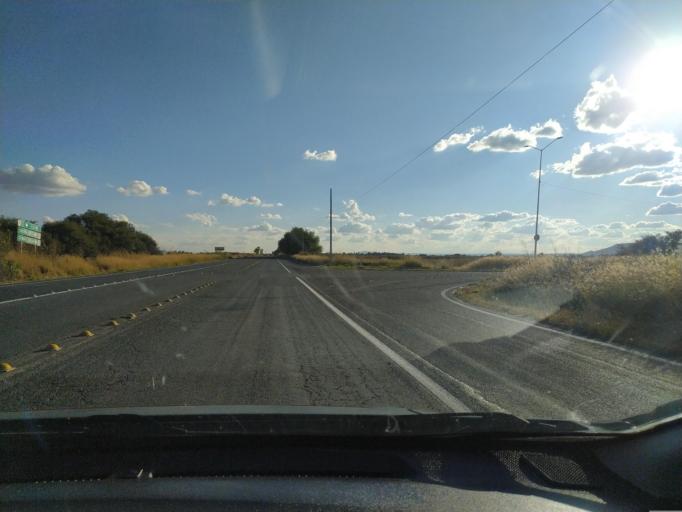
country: MX
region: Guanajuato
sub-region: San Francisco del Rincon
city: Fraccionamiento la Mezquitera
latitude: 21.0119
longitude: -101.8280
